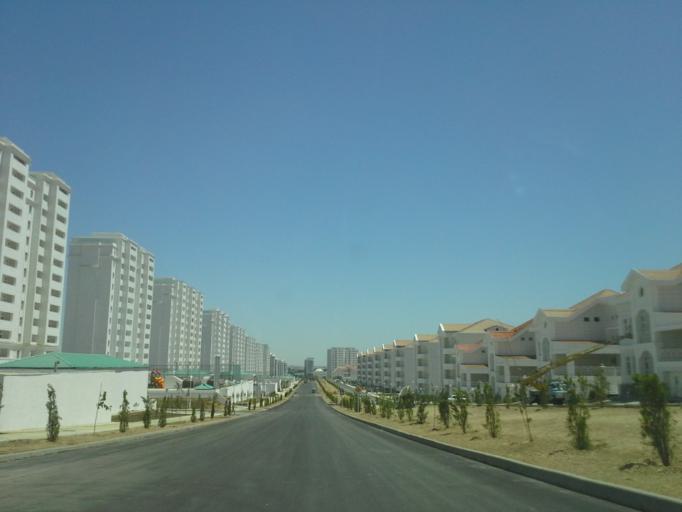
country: TM
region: Ahal
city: Ashgabat
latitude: 37.9392
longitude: 58.3496
